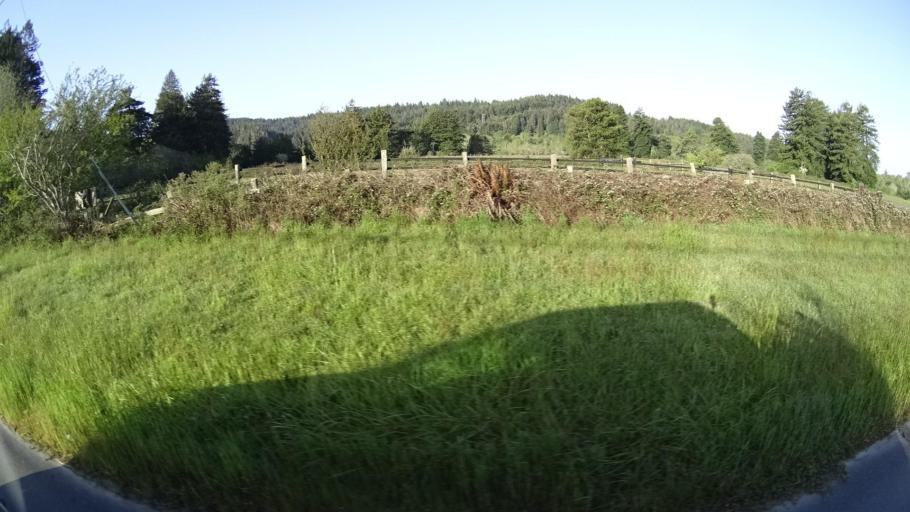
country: US
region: California
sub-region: Humboldt County
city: Myrtletown
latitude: 40.7792
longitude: -124.0754
